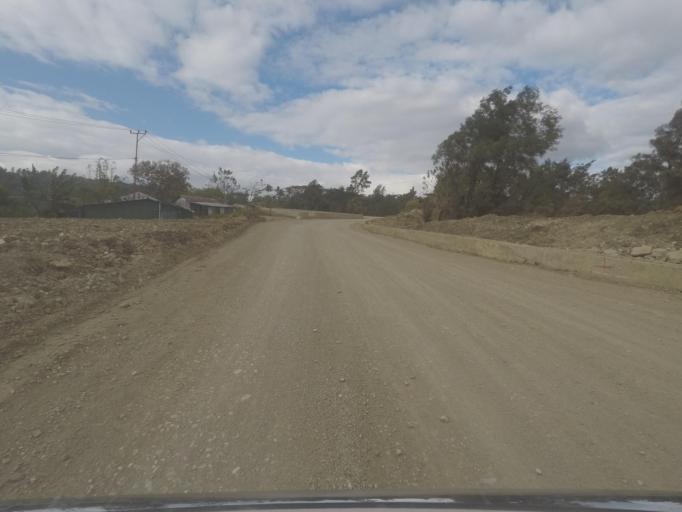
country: TL
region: Baucau
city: Venilale
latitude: -8.6350
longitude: 126.3773
